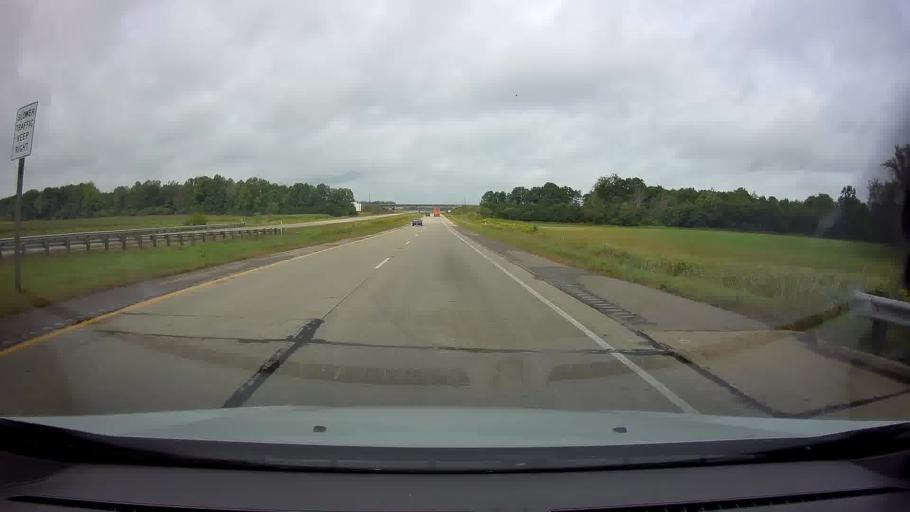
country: US
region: Wisconsin
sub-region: Shawano County
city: Shawano
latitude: 44.7658
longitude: -88.6312
